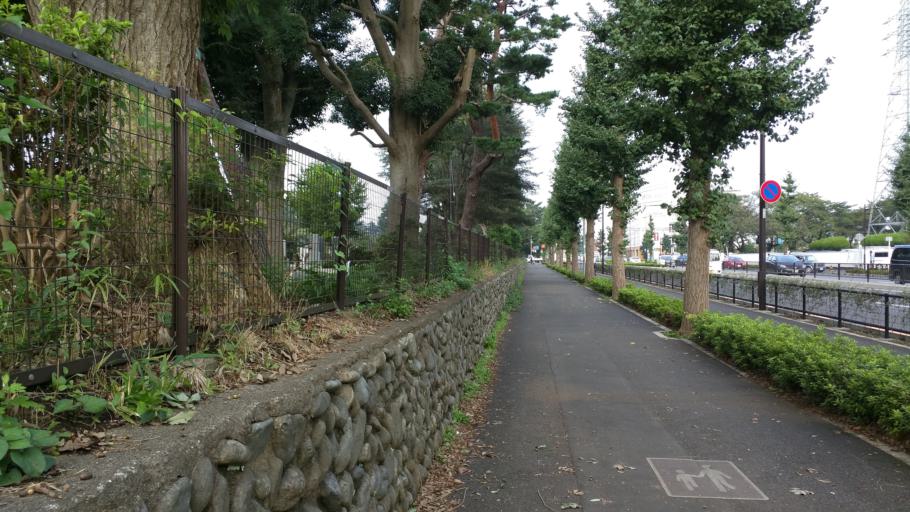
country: JP
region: Tokyo
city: Kokubunji
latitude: 35.6880
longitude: 139.5148
